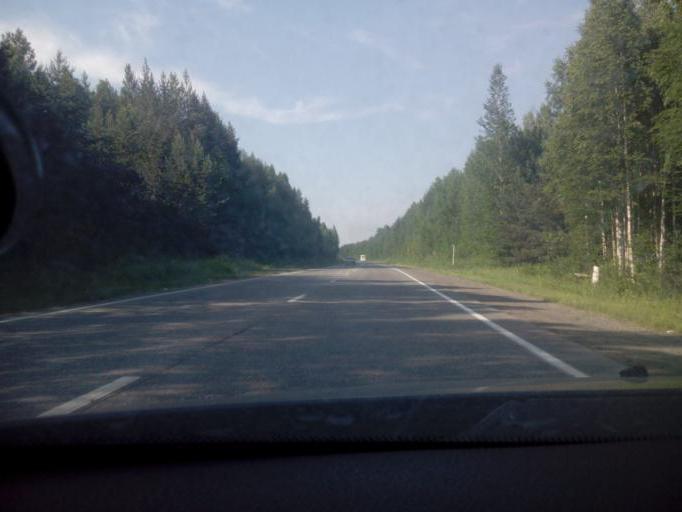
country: RU
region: Sverdlovsk
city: Verkh-Neyvinskiy
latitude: 57.2682
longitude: 60.2936
